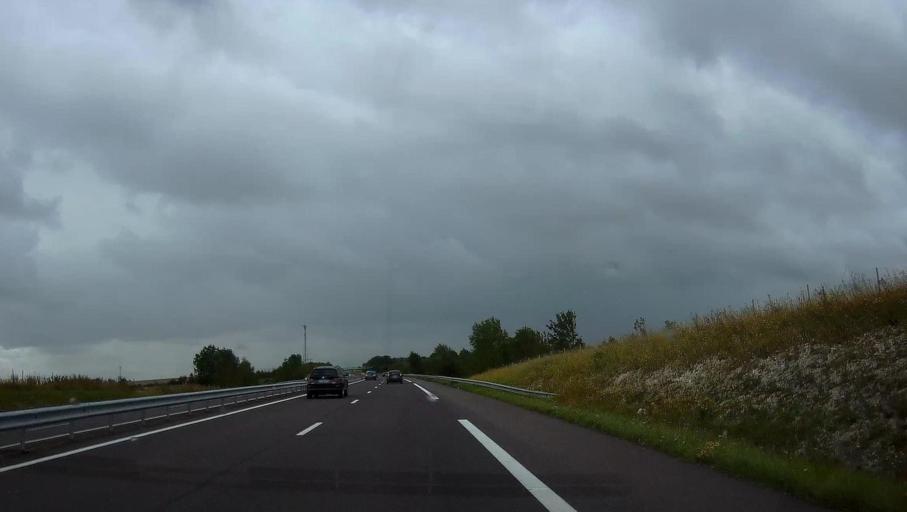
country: FR
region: Champagne-Ardenne
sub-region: Departement de l'Aube
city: Mailly-le-Camp
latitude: 48.6641
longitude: 4.1706
